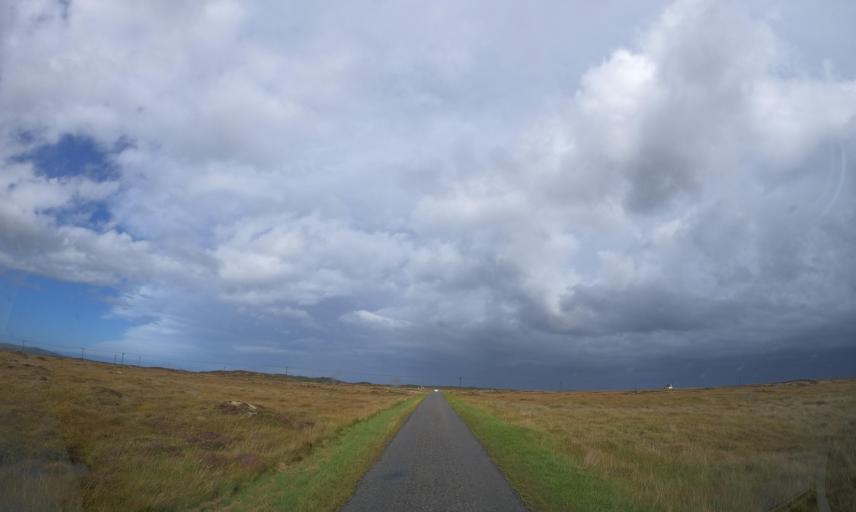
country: GB
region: Scotland
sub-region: Eilean Siar
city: Barra
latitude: 56.5166
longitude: -6.8349
